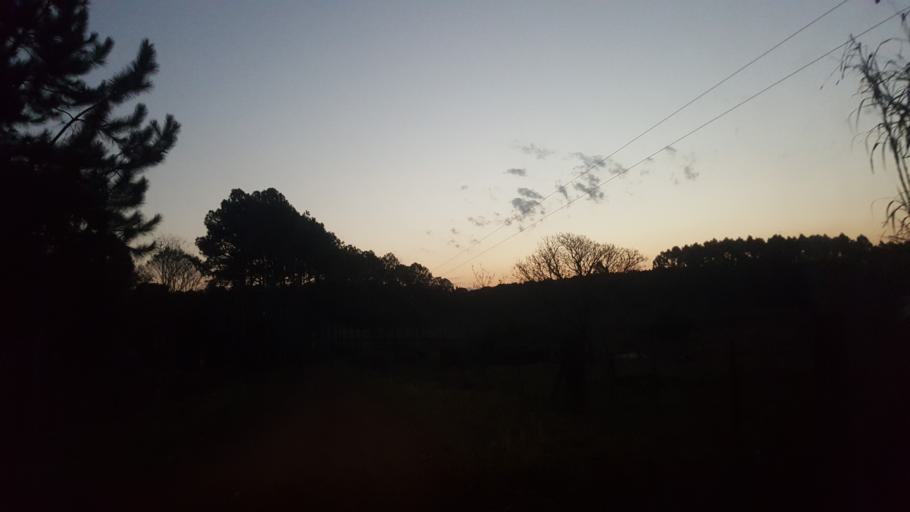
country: AR
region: Misiones
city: Capiovi
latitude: -26.9028
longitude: -55.0520
